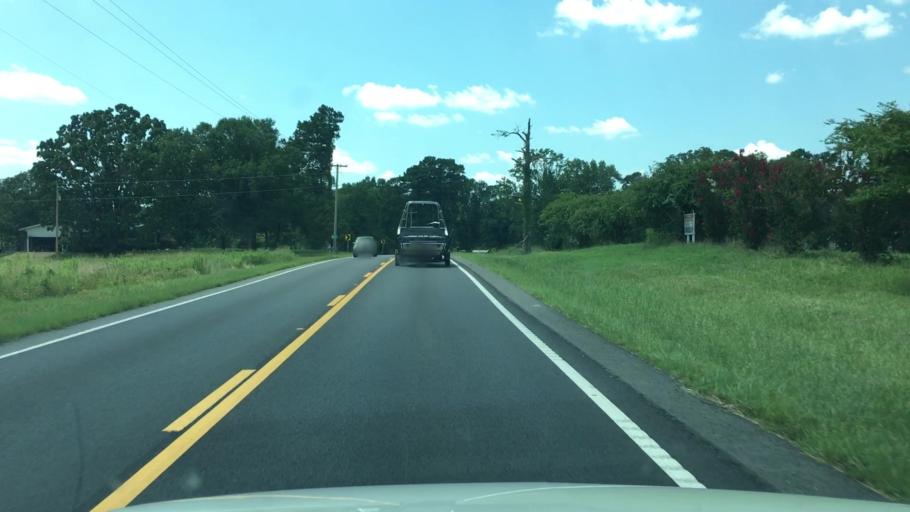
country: US
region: Arkansas
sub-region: Garland County
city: Lake Hamilton
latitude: 34.2811
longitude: -93.1608
